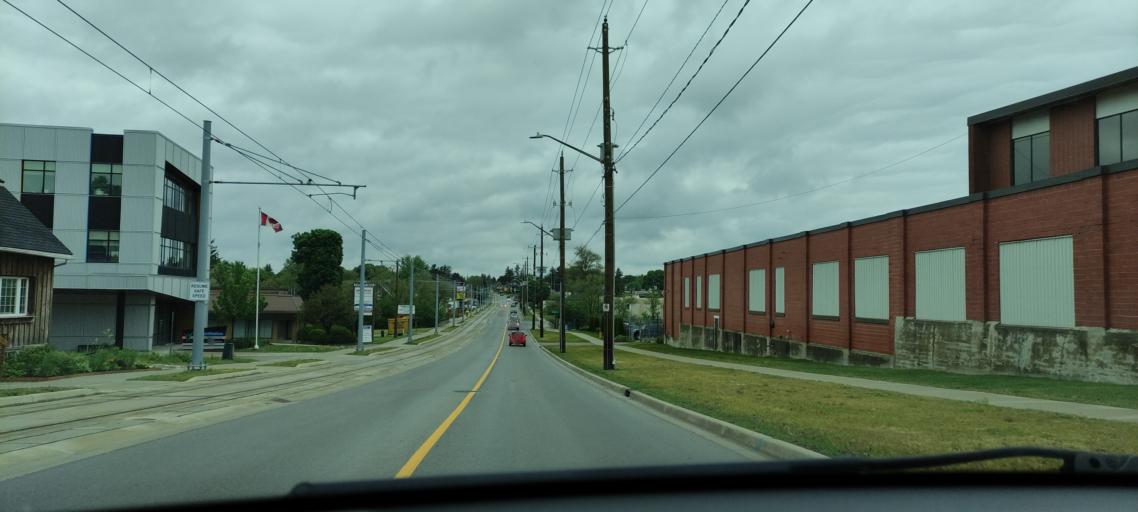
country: CA
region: Ontario
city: Kitchener
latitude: 43.4400
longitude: -80.4736
